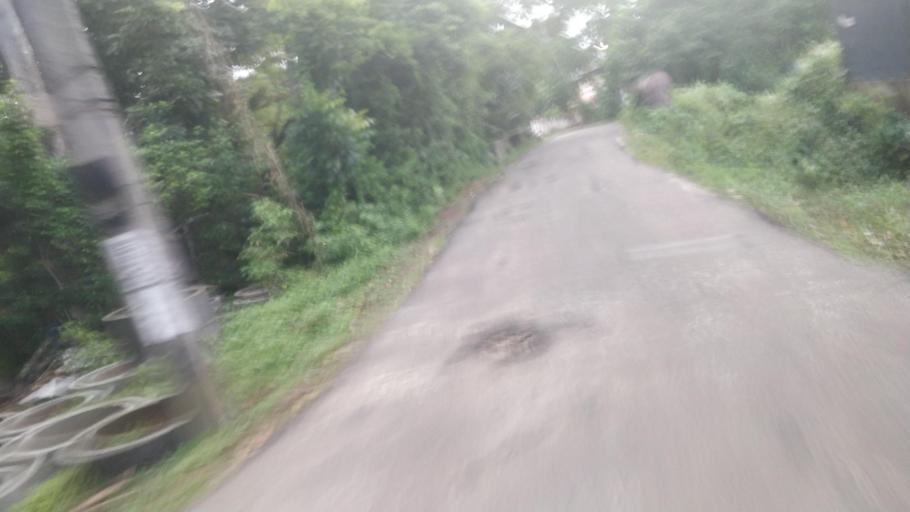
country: IN
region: Kerala
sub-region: Alappuzha
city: Shertallai
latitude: 9.6899
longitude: 76.3536
